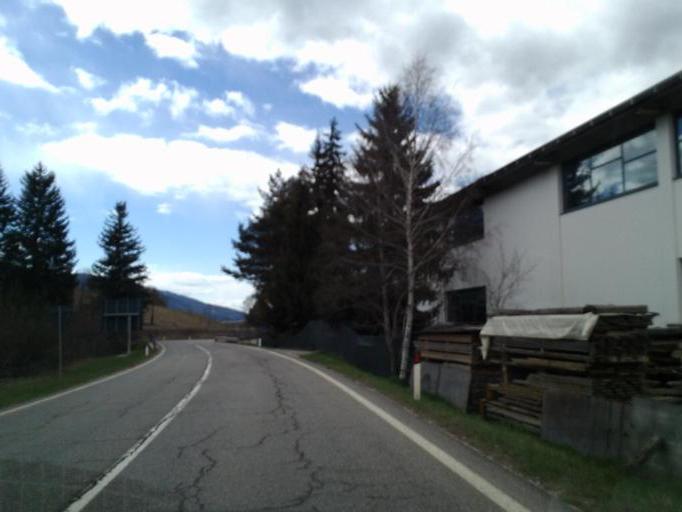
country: IT
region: Trentino-Alto Adige
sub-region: Bolzano
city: Dobbiaco
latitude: 46.7327
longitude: 12.1991
